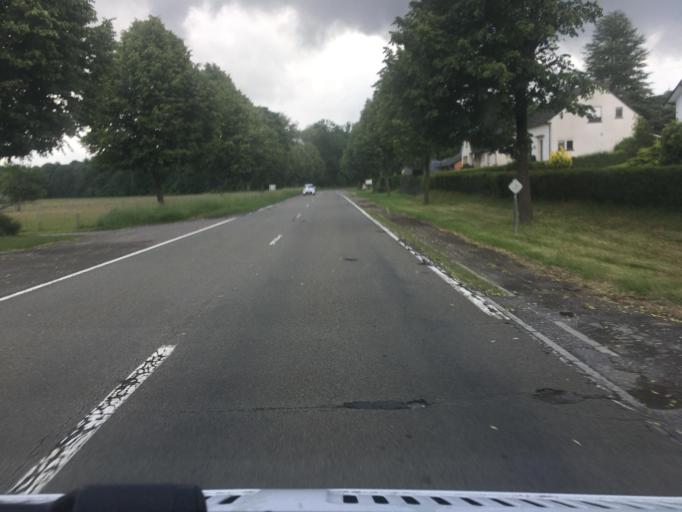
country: BE
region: Wallonia
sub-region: Province du Luxembourg
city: Florenville
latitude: 49.6831
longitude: 5.3321
